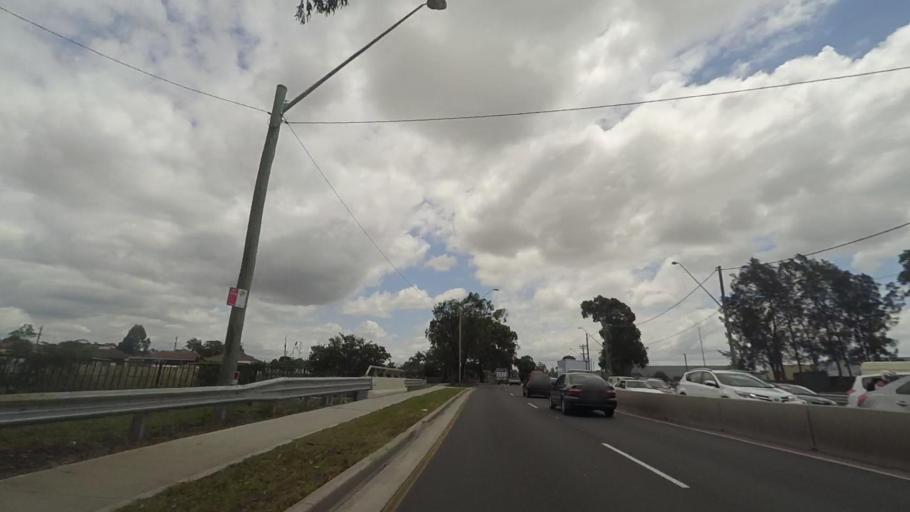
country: AU
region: New South Wales
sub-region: Fairfield
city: Liverpool
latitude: -33.9148
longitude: 150.9204
